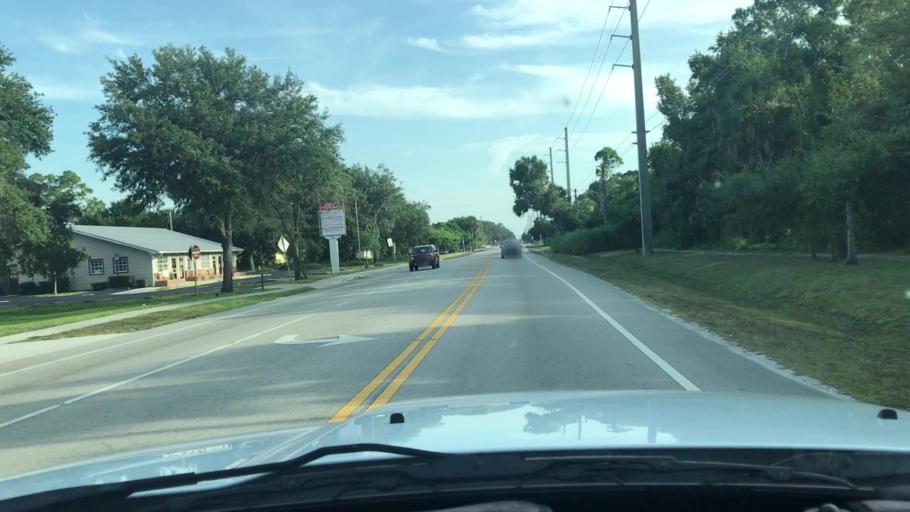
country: US
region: Florida
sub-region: Indian River County
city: Vero Beach South
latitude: 27.5950
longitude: -80.4141
